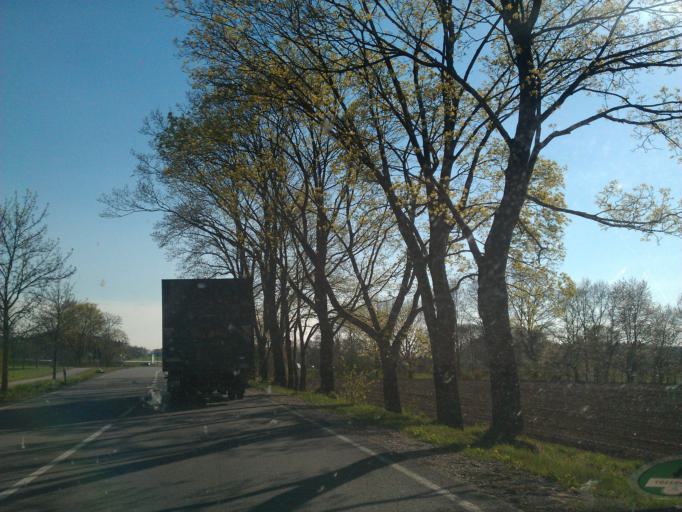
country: DE
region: Bavaria
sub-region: Swabia
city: Aichach
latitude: 48.4357
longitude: 11.1064
